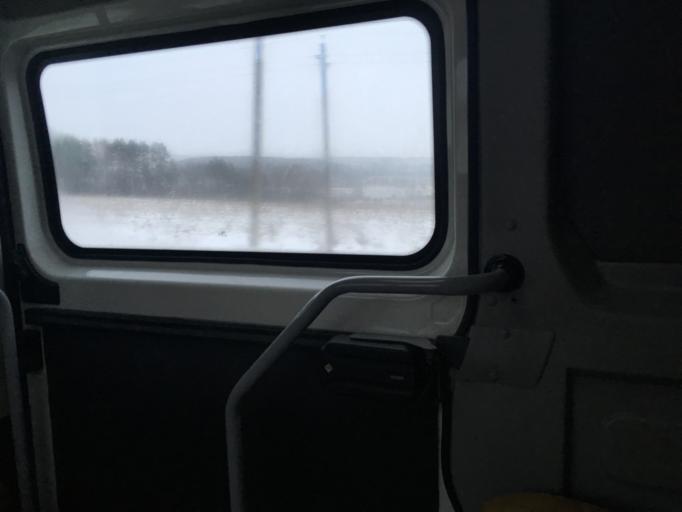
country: RU
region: Tula
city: Dubna
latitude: 54.0908
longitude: 37.0780
